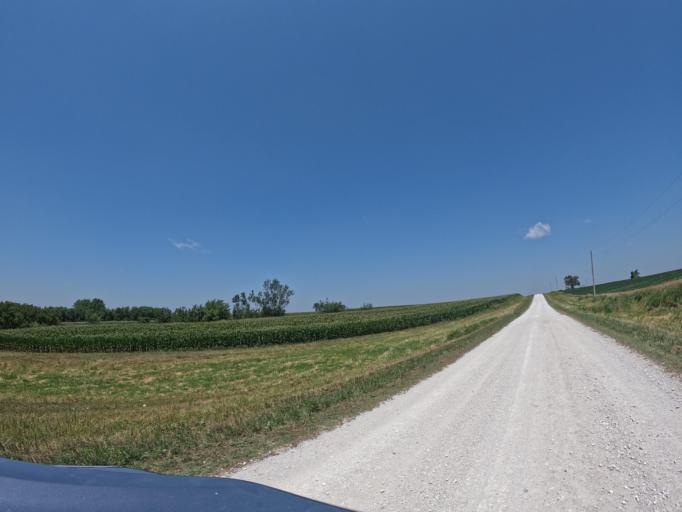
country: US
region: Iowa
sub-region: Keokuk County
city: Sigourney
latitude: 41.2620
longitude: -92.1697
